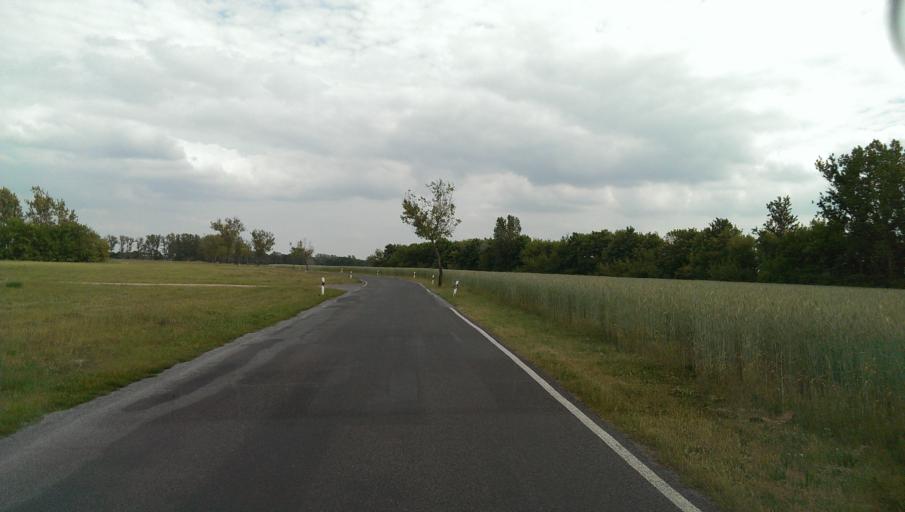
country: DE
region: Brandenburg
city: Linthe
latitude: 52.1533
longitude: 12.8216
